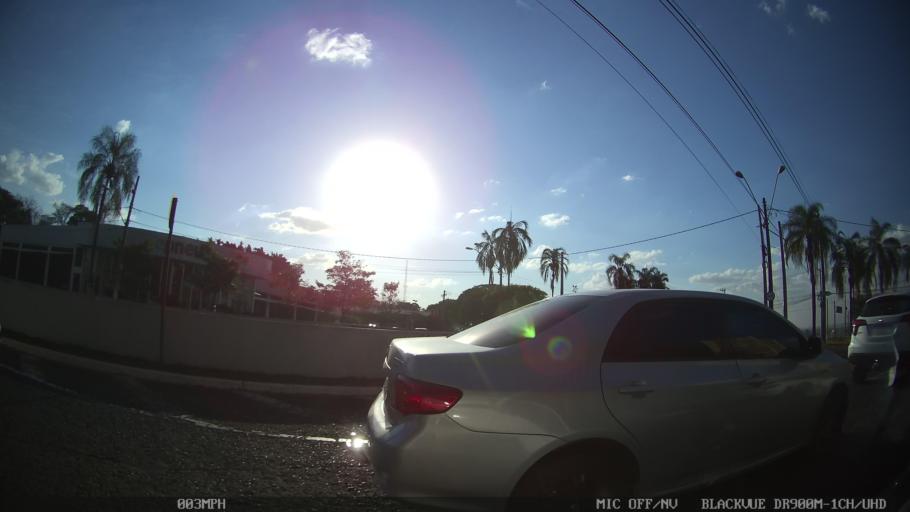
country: BR
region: Sao Paulo
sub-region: Ribeirao Preto
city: Ribeirao Preto
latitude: -21.1746
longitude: -47.7948
